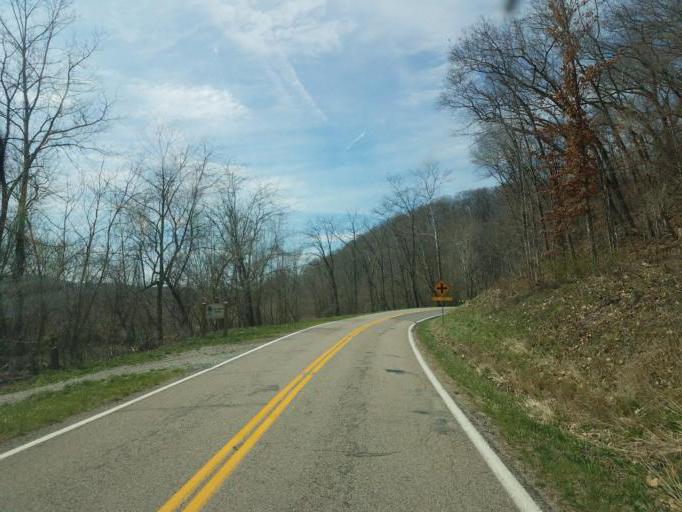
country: US
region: Ohio
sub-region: Knox County
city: Oak Hill
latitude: 40.3771
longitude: -82.1982
